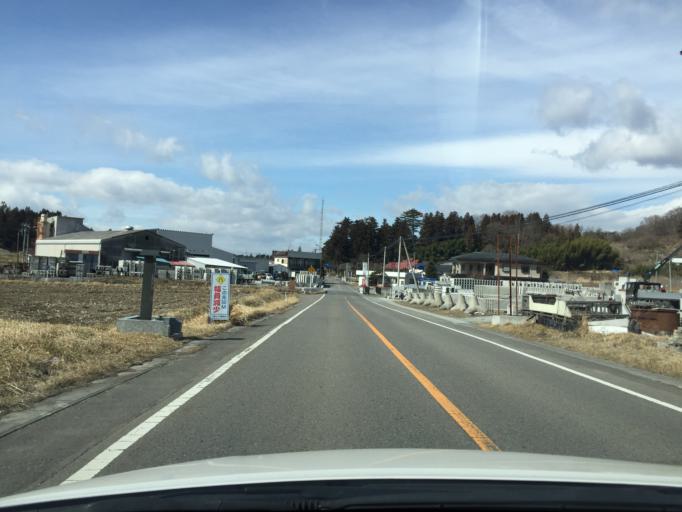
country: JP
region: Fukushima
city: Funehikimachi-funehiki
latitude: 37.3934
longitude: 140.5757
